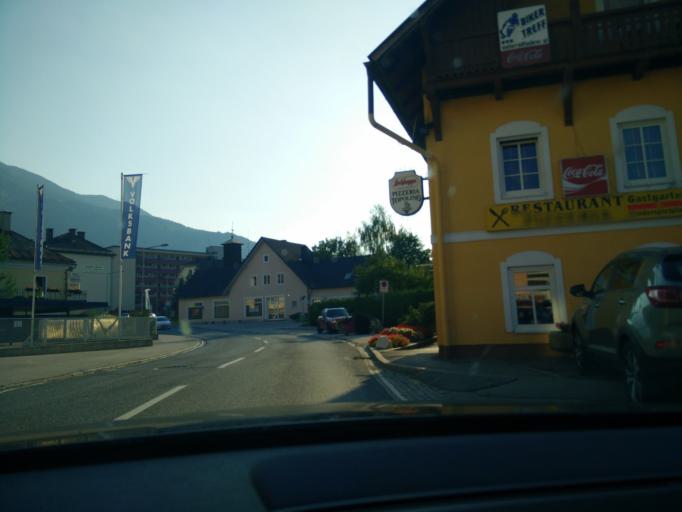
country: AT
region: Carinthia
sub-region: Politischer Bezirk Klagenfurt Land
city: Ferlach
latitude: 46.5273
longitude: 14.3003
